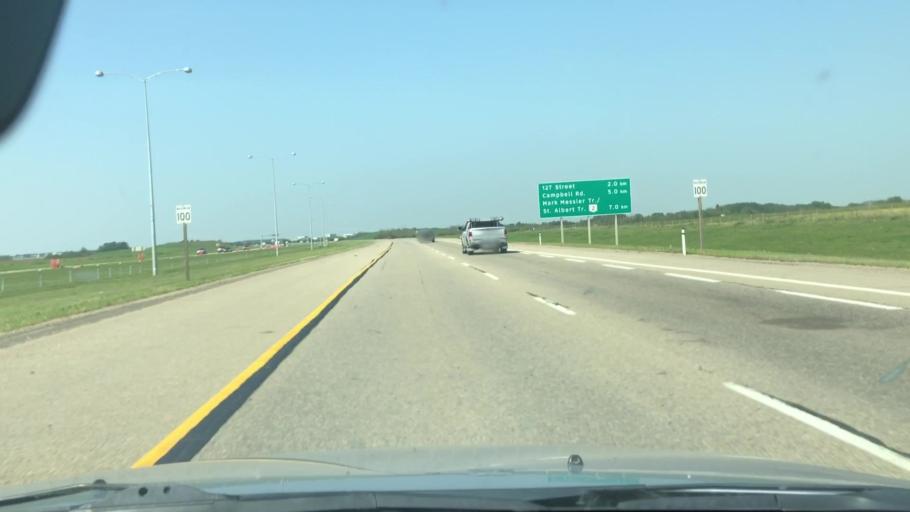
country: CA
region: Alberta
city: Edmonton
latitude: 53.6471
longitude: -113.5050
